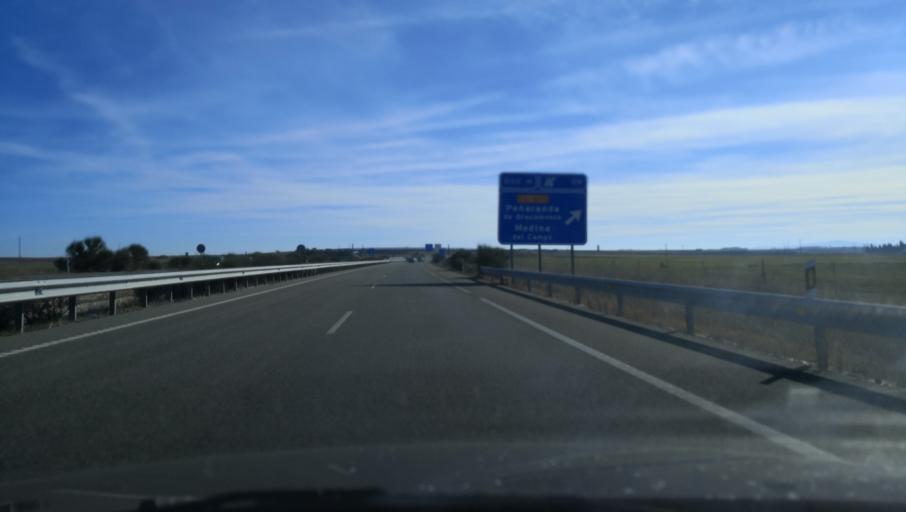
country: ES
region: Castille and Leon
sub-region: Provincia de Salamanca
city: Penaranda de Bracamonte
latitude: 40.9195
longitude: -5.2026
